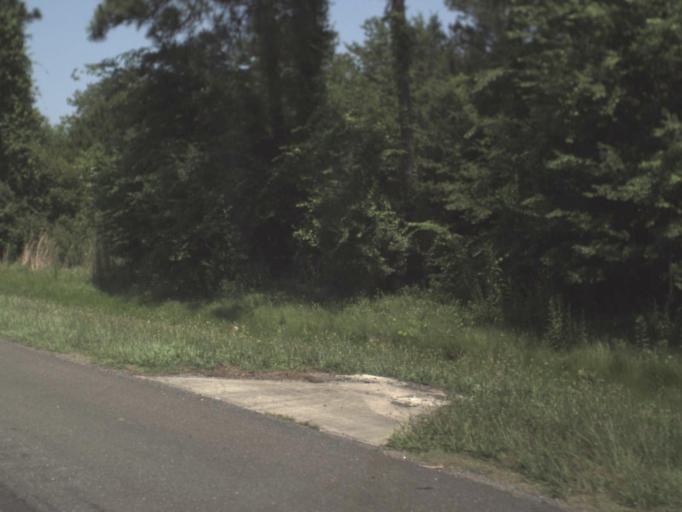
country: US
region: Florida
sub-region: Duval County
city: Baldwin
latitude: 30.3074
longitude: -81.8728
